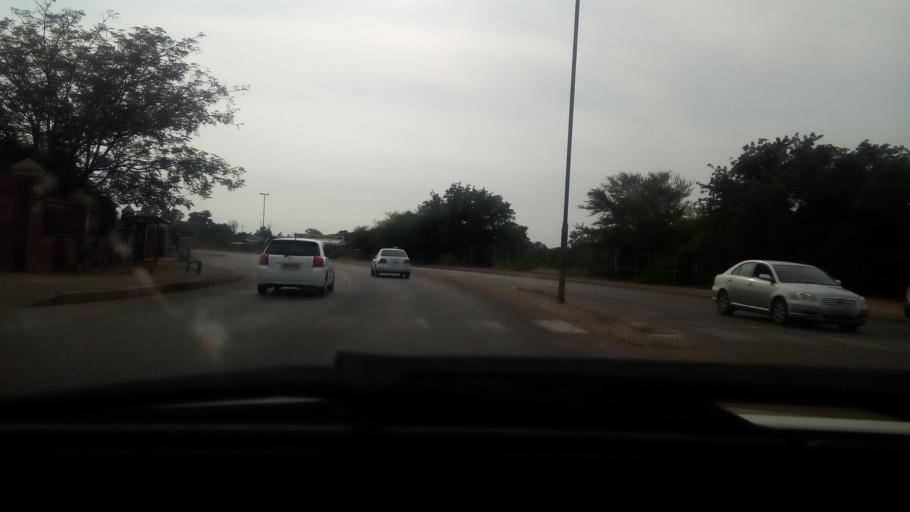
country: BW
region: South East
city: Gaborone
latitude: -24.6657
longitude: 25.9314
